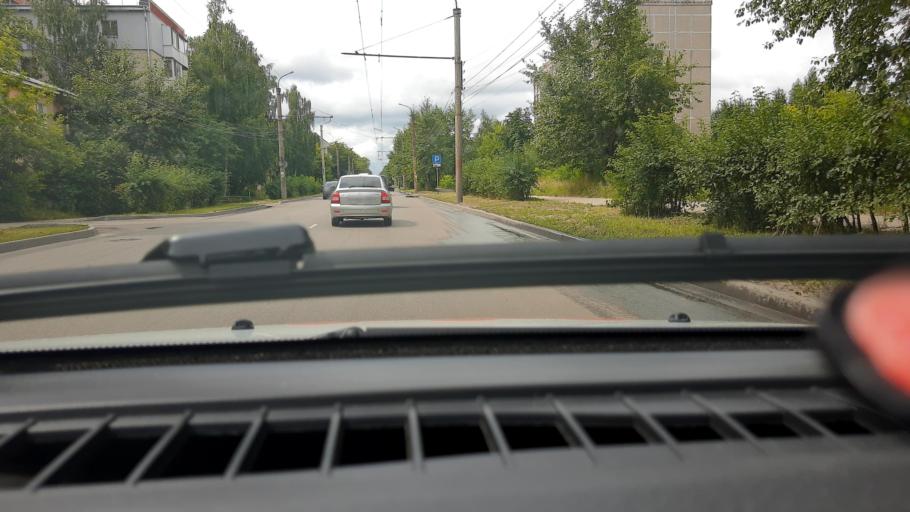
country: RU
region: Nizjnij Novgorod
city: Dzerzhinsk
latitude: 56.2342
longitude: 43.4745
